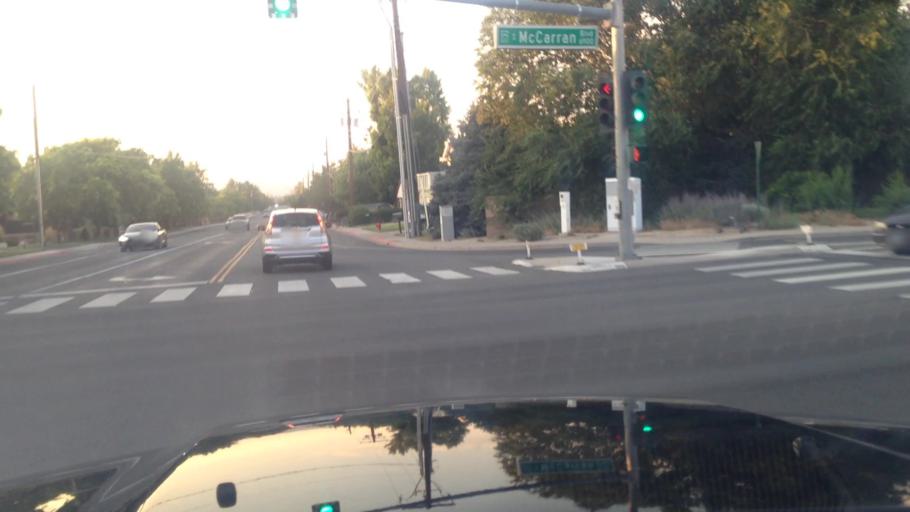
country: US
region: Nevada
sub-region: Washoe County
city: Reno
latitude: 39.4765
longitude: -119.8079
